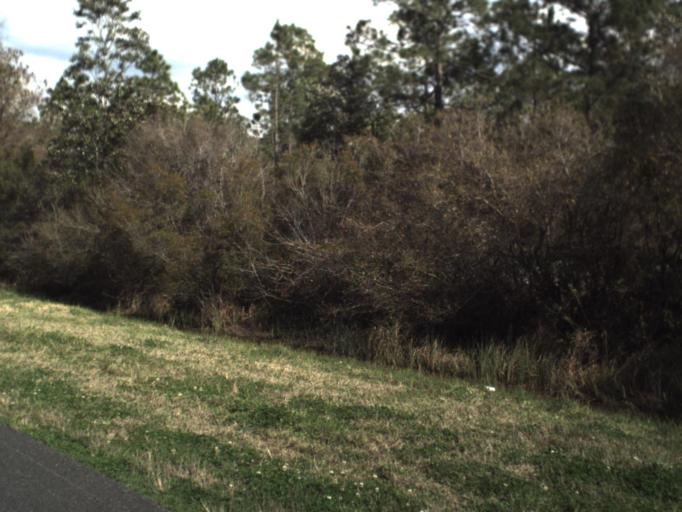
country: US
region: Florida
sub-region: Bay County
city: Youngstown
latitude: 30.2938
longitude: -85.4933
